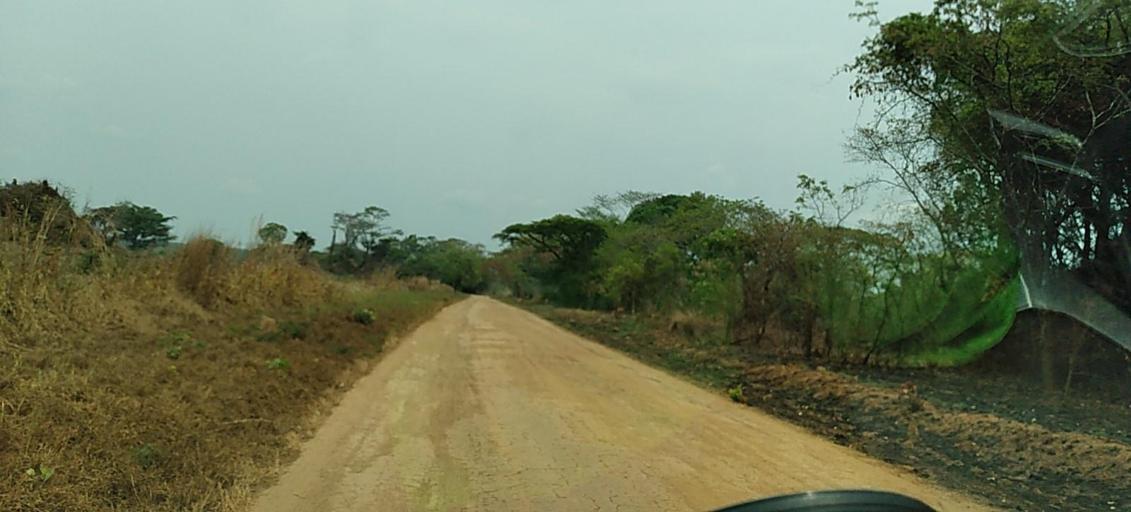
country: ZM
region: North-Western
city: Solwezi
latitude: -12.7889
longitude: 26.5283
